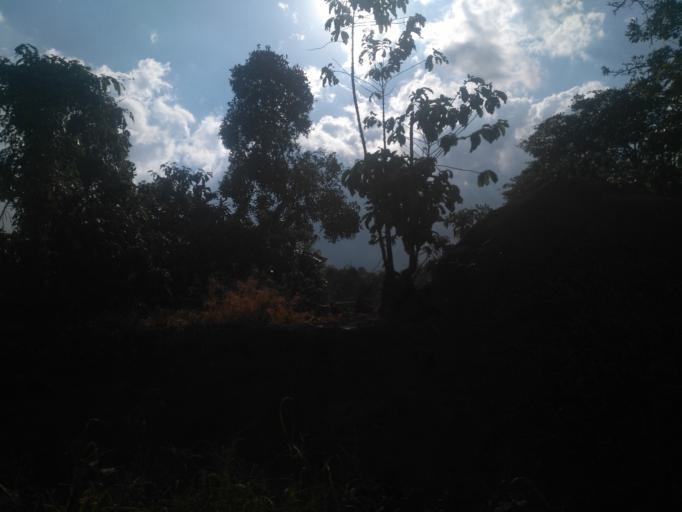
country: UG
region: Central Region
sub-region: Wakiso District
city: Kajansi
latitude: 0.2644
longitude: 32.4382
